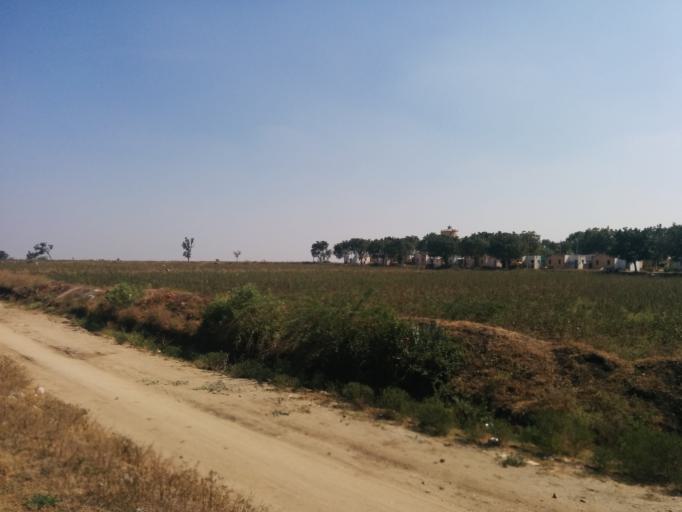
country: IN
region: Karnataka
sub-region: Gadag
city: Gadag
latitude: 15.4382
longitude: 75.6617
